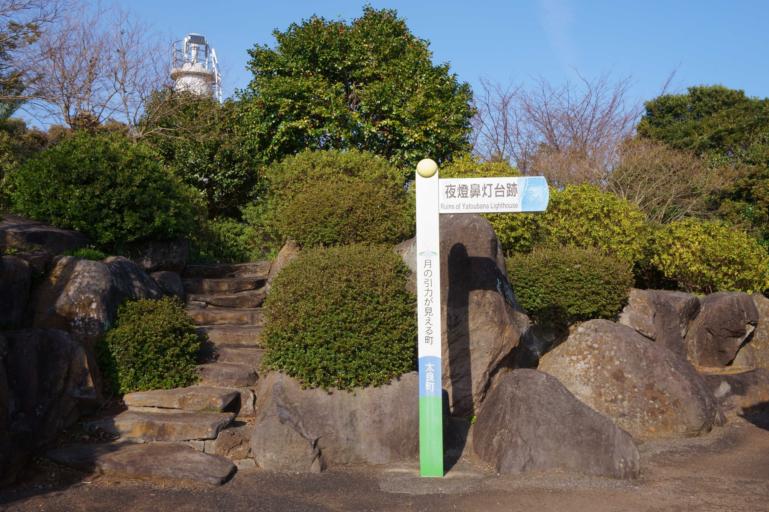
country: JP
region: Saga Prefecture
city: Kashima
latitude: 32.9566
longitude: 130.2245
